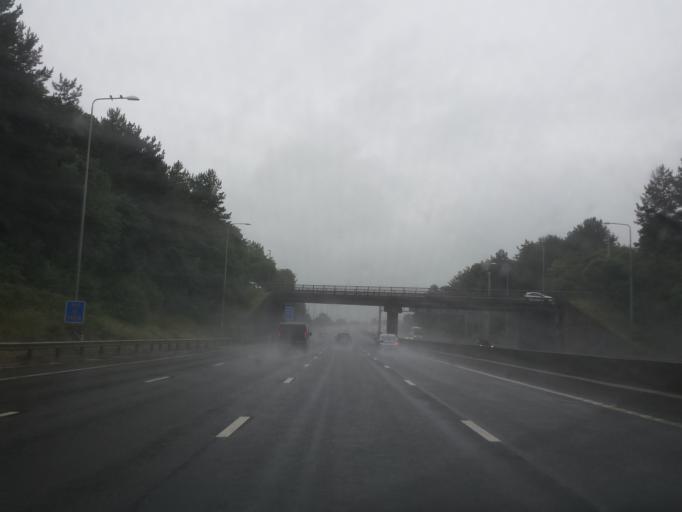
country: GB
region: England
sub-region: Nottinghamshire
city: Kimberley
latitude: 52.9493
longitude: -1.2776
